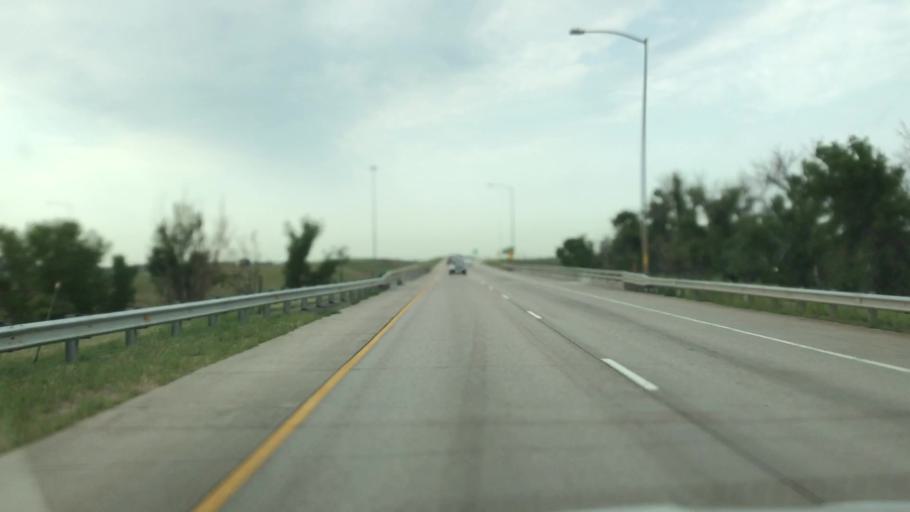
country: US
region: Colorado
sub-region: Adams County
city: Aurora
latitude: 39.8045
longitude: -104.7872
